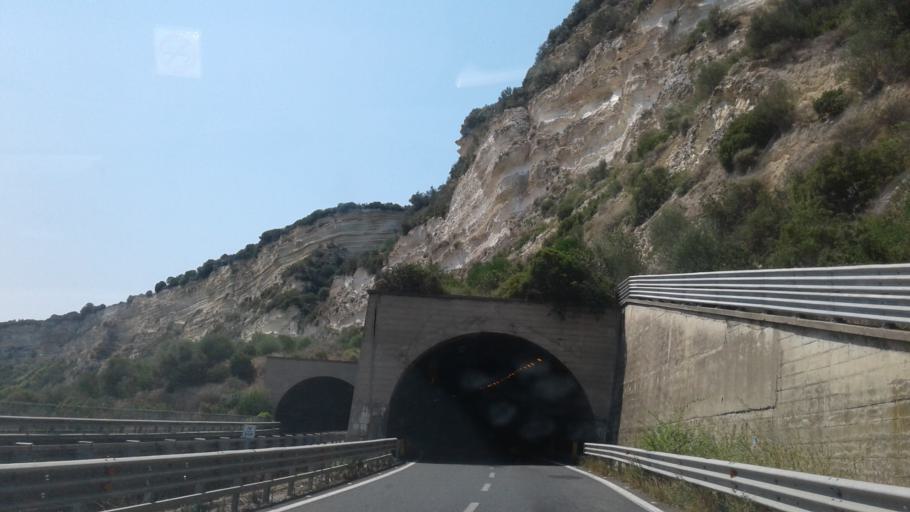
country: IT
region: Sardinia
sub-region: Provincia di Sassari
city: Ossi
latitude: 40.7013
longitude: 8.5891
